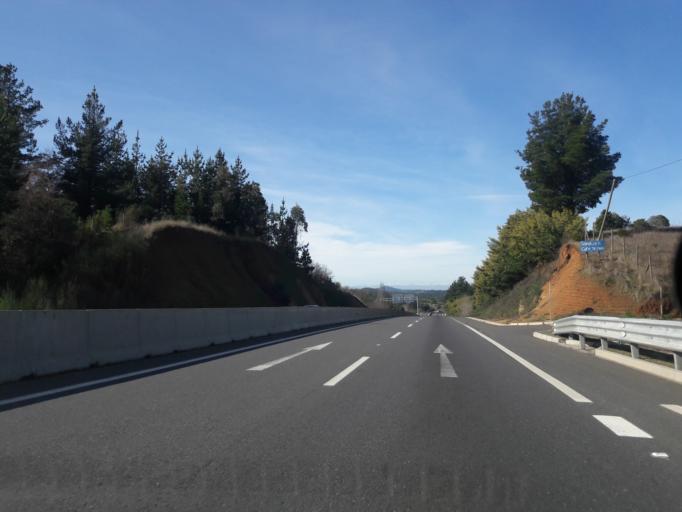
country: CL
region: Biobio
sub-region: Provincia de Biobio
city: Yumbel
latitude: -36.9638
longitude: -72.7064
